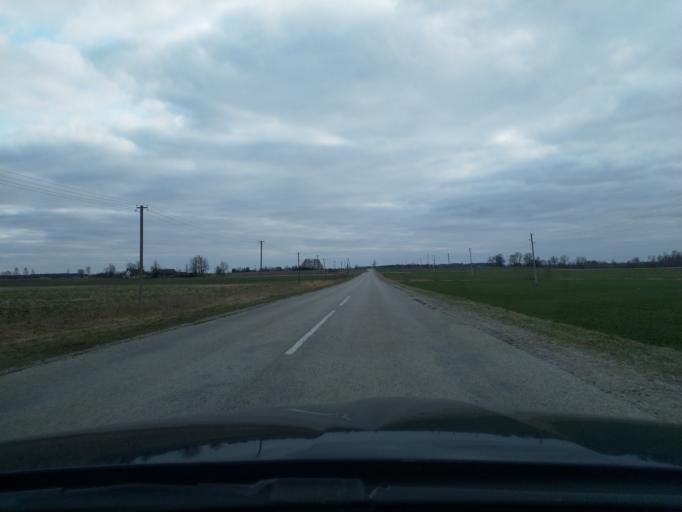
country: LV
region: Talsu Rajons
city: Sabile
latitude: 56.9585
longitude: 22.6134
